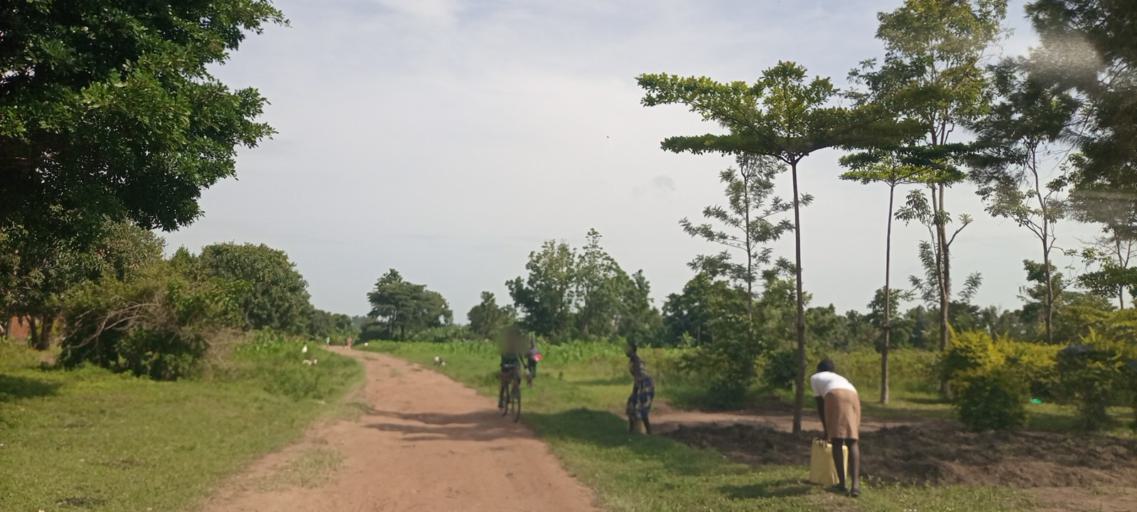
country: UG
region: Eastern Region
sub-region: Budaka District
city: Budaka
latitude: 1.1358
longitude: 34.0167
